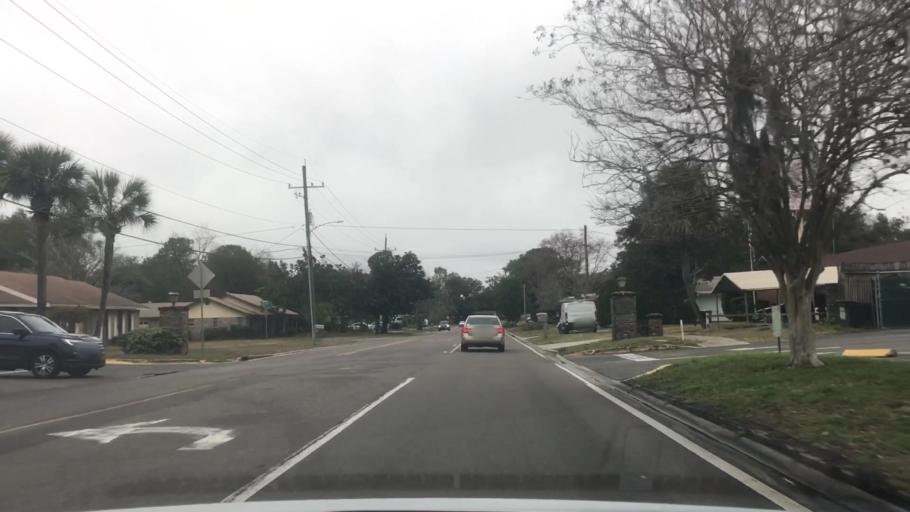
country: US
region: Florida
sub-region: Duval County
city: Jacksonville
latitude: 30.3538
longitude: -81.5780
